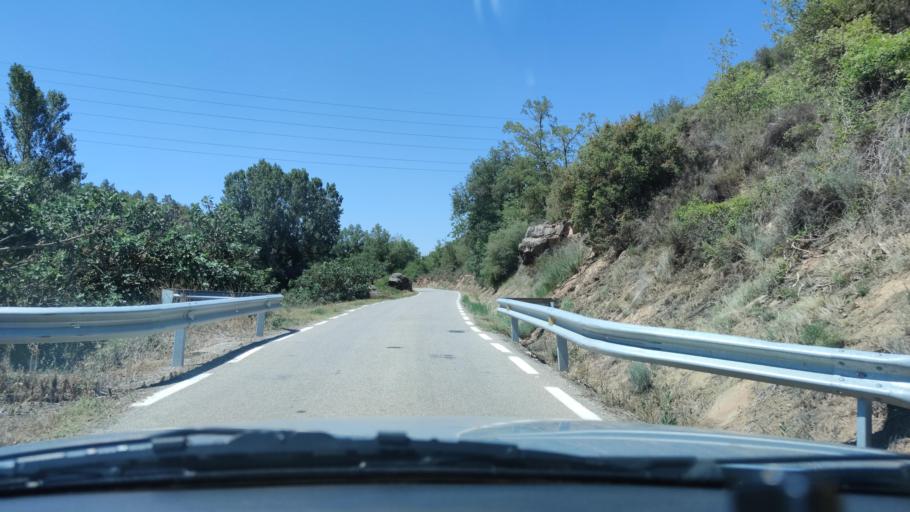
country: ES
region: Catalonia
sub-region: Provincia de Lleida
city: Tora de Riubregos
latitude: 41.8236
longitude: 1.4207
